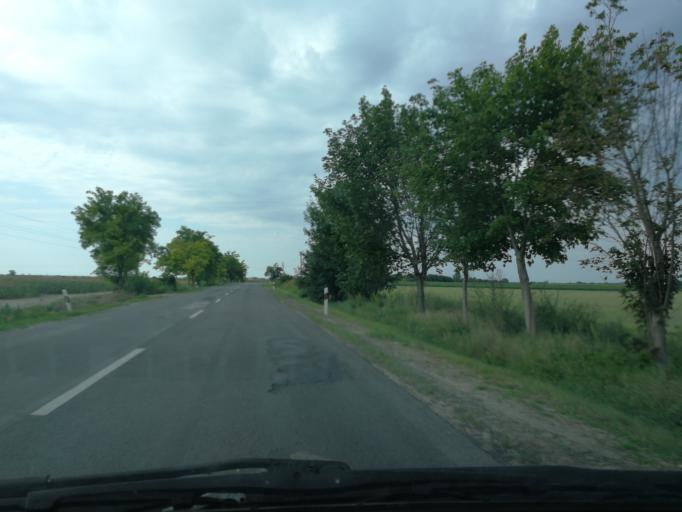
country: HU
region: Bacs-Kiskun
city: Batya
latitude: 46.4491
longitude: 18.9534
